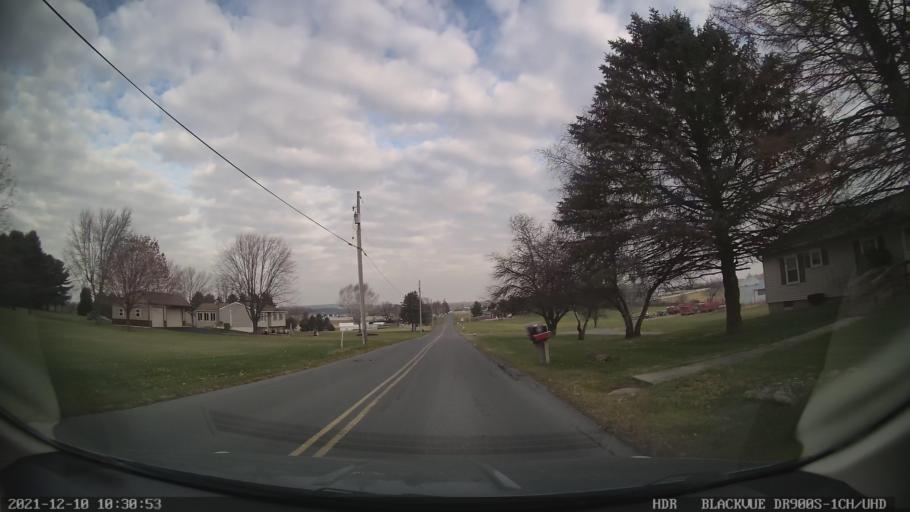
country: US
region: Pennsylvania
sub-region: Berks County
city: Topton
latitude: 40.5190
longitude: -75.7196
